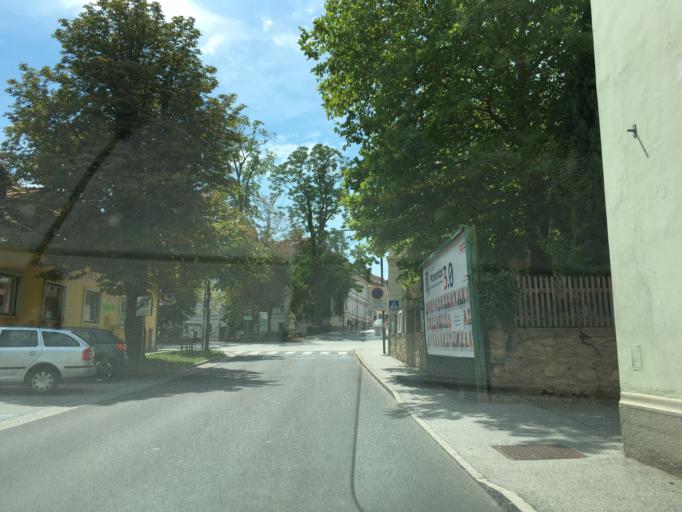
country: AT
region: Styria
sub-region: Politischer Bezirk Hartberg-Fuerstenfeld
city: Hartberg
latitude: 47.2826
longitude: 15.9725
